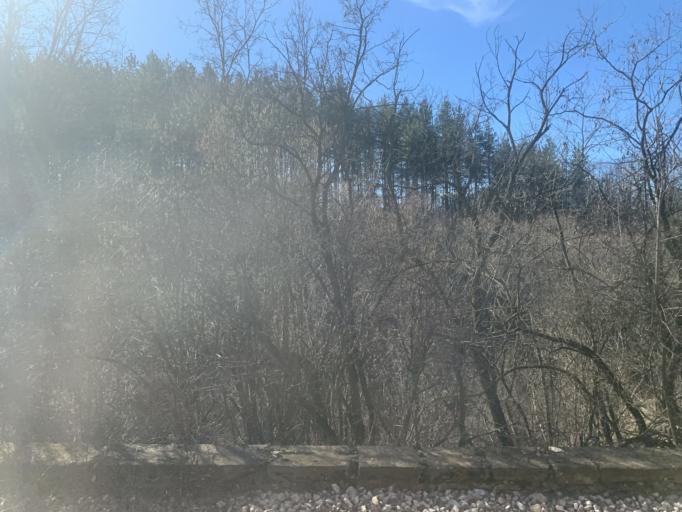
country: BG
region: Sofiya
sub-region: Obshtina Gorna Malina
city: Gorna Malina
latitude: 42.5654
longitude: 23.6819
